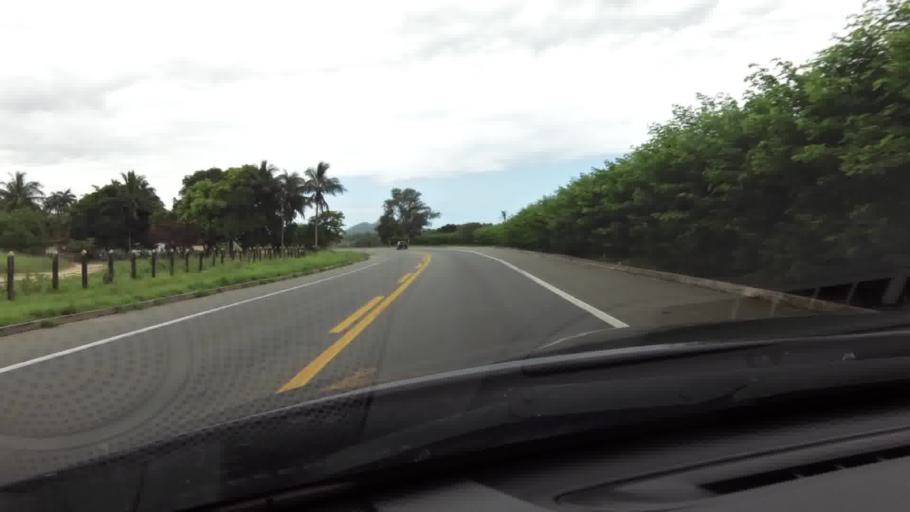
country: BR
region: Espirito Santo
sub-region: Guarapari
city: Guarapari
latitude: -20.6046
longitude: -40.5037
